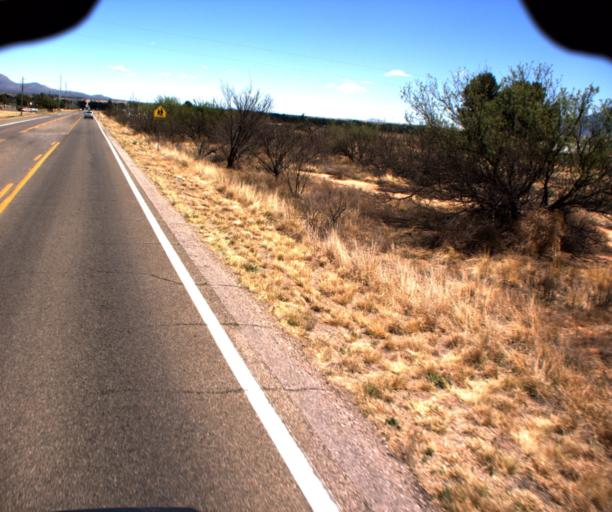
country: US
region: Arizona
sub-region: Cochise County
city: Sierra Vista Southeast
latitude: 31.3799
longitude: -110.1270
